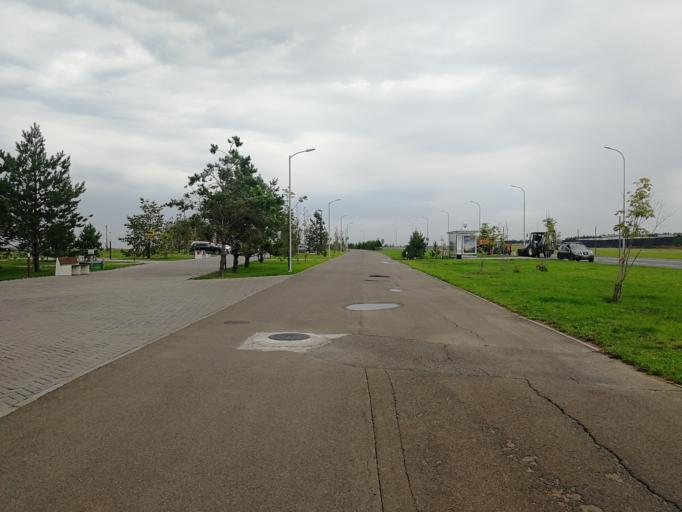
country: RU
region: Tatarstan
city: Sviyazhsk
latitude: 55.7517
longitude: 48.7448
